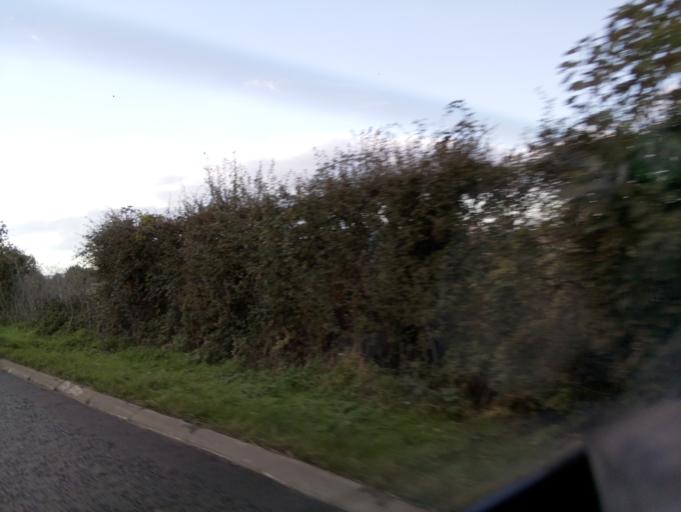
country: GB
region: England
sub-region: Herefordshire
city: Ocle Pychard
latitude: 52.0649
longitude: -2.5656
